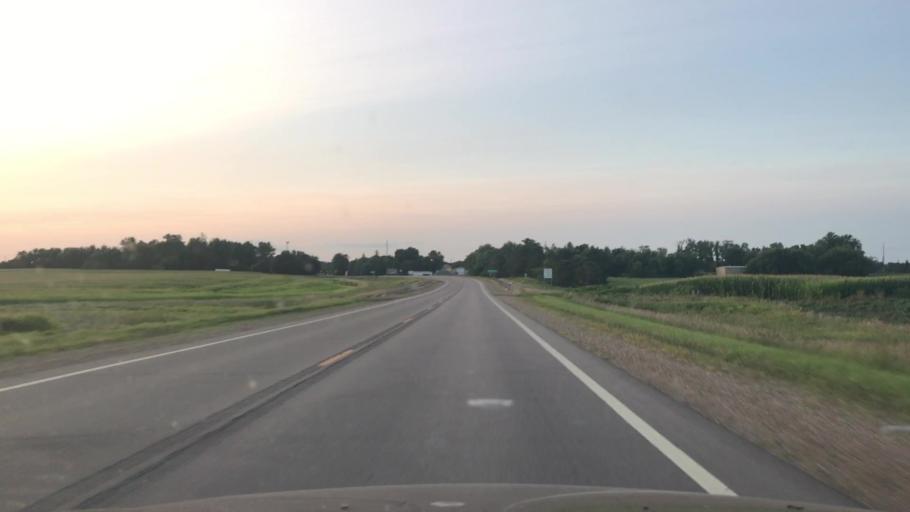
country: US
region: Minnesota
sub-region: Redwood County
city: Redwood Falls
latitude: 44.5208
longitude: -95.1180
